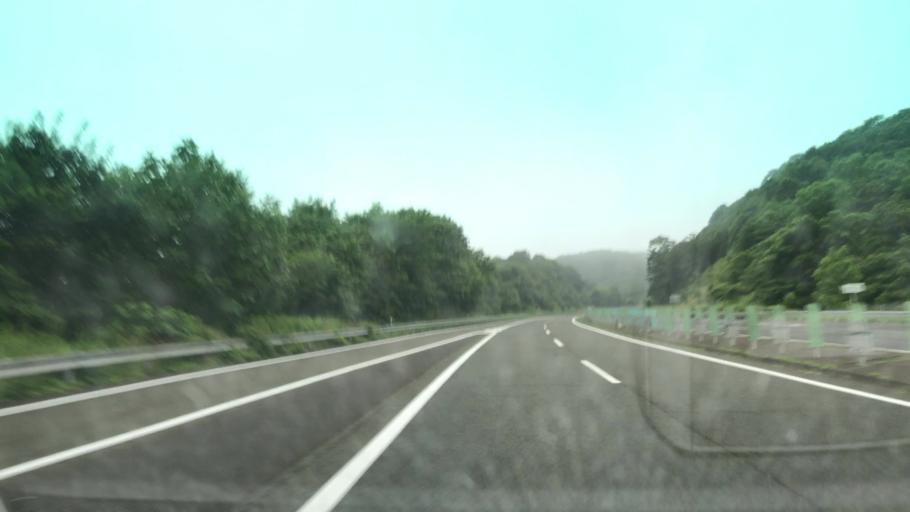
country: JP
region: Hokkaido
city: Shiraoi
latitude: 42.4989
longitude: 141.2616
